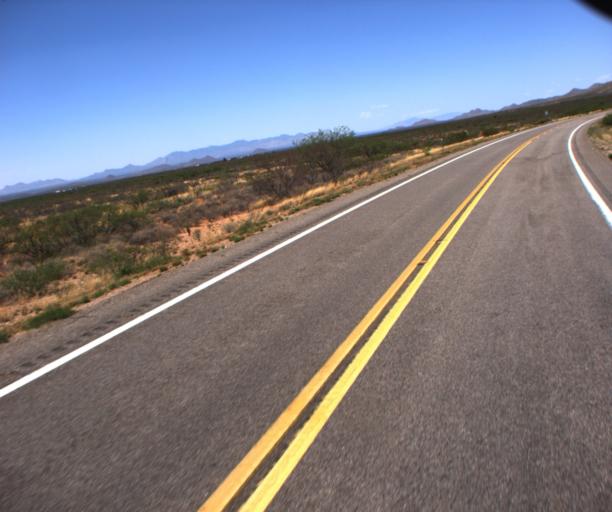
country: US
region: Arizona
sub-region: Cochise County
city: Tombstone
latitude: 31.5659
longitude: -110.0258
